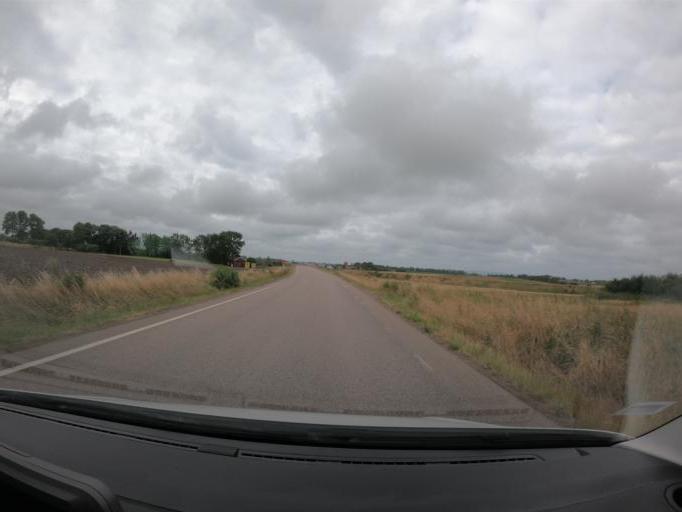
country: SE
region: Skane
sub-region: Bastads Kommun
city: Forslov
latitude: 56.3457
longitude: 12.8038
